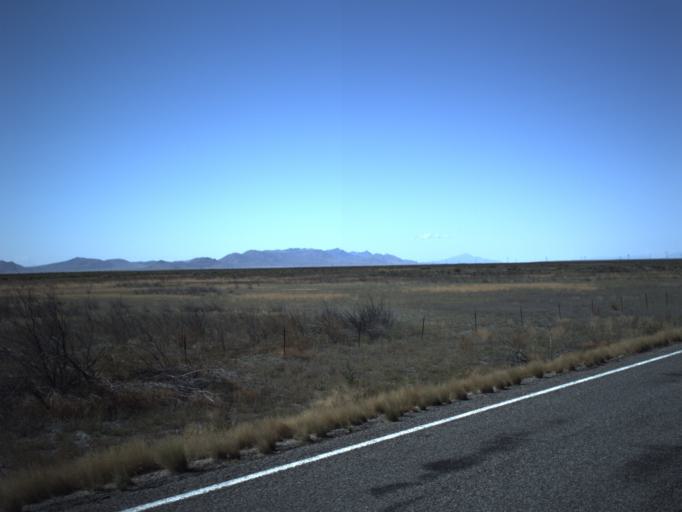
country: US
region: Utah
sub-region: Millard County
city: Delta
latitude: 39.2712
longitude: -112.8616
